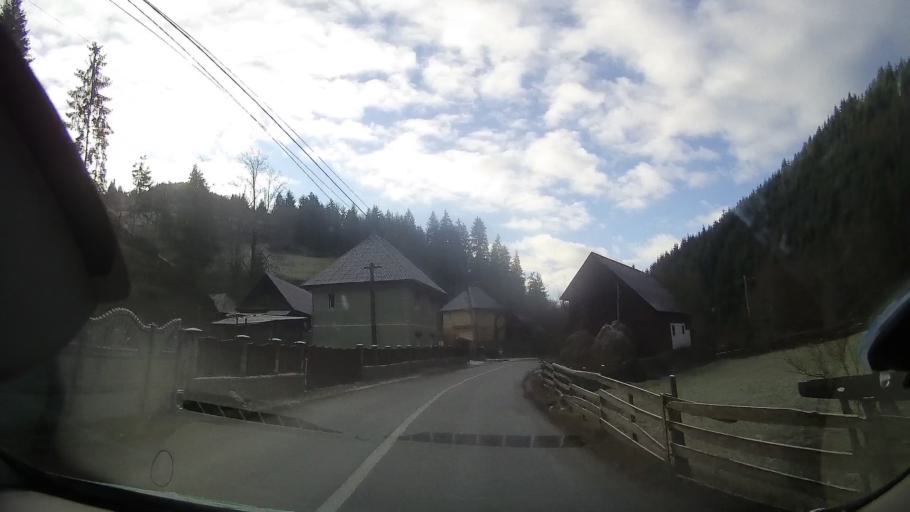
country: RO
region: Alba
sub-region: Comuna Albac
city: Albac
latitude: 46.4573
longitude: 22.9753
